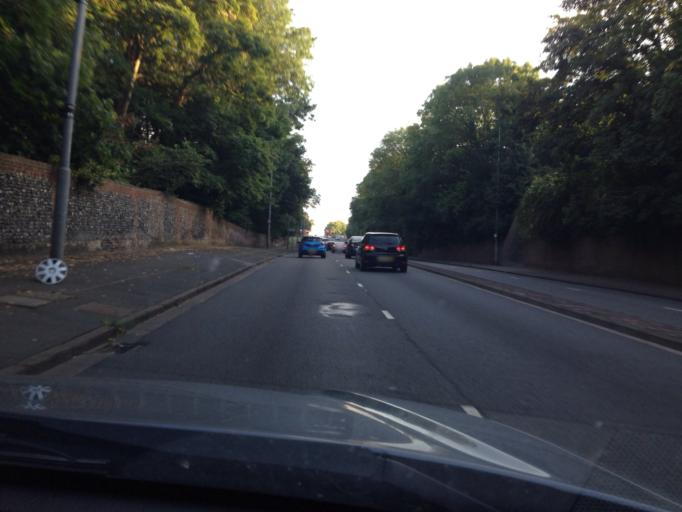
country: GB
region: England
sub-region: Buckinghamshire
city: High Wycombe
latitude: 51.6219
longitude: -0.7570
